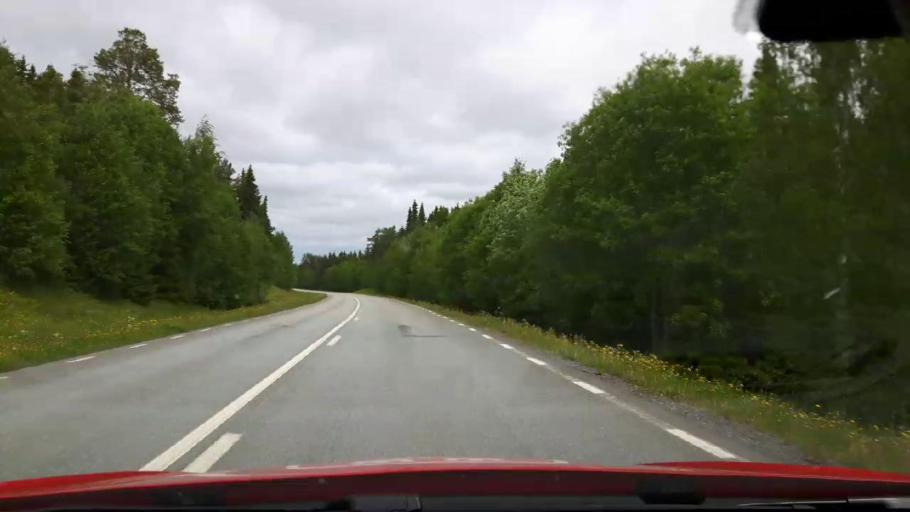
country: SE
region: Jaemtland
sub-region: Krokoms Kommun
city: Krokom
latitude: 63.3645
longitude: 14.5061
